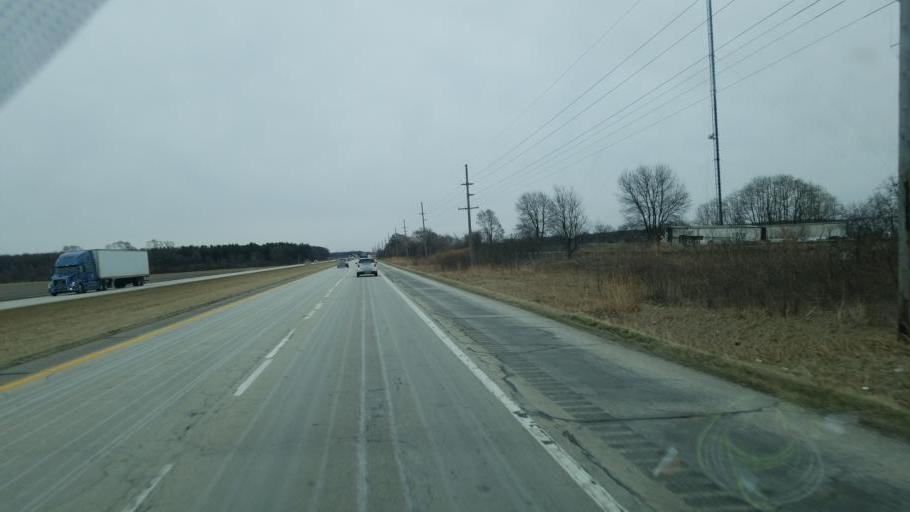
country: US
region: Indiana
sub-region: Starke County
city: Koontz Lake
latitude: 41.3777
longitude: -86.5495
